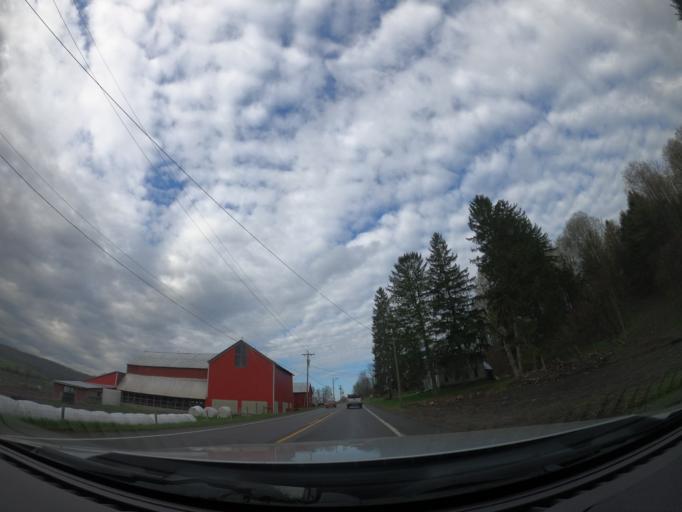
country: US
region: New York
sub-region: Cortland County
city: McGraw
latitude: 42.6829
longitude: -76.0606
